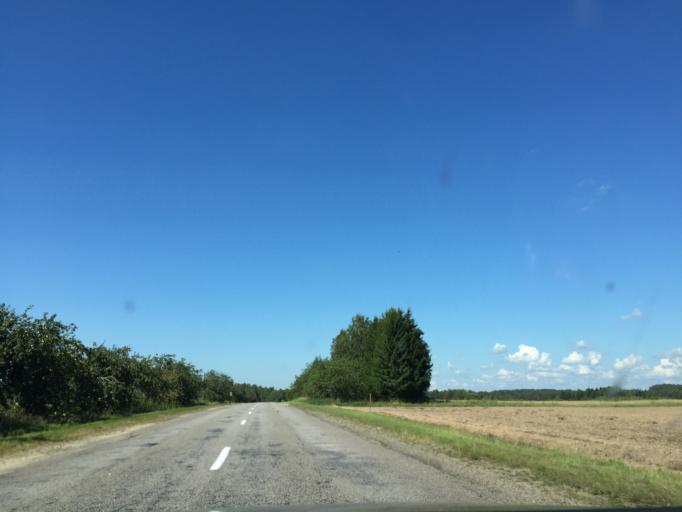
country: LV
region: Limbazu Rajons
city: Limbazi
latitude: 57.4590
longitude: 24.7203
